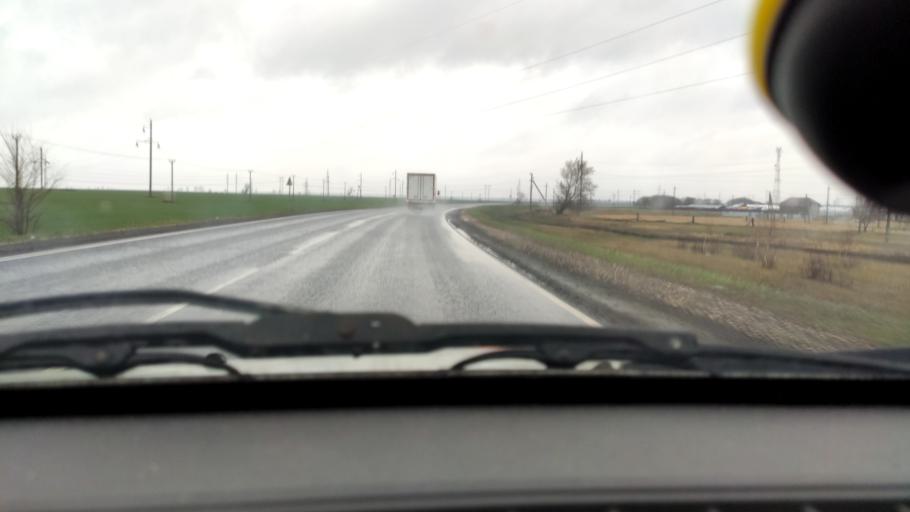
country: RU
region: Samara
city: Povolzhskiy
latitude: 53.6338
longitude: 49.6587
